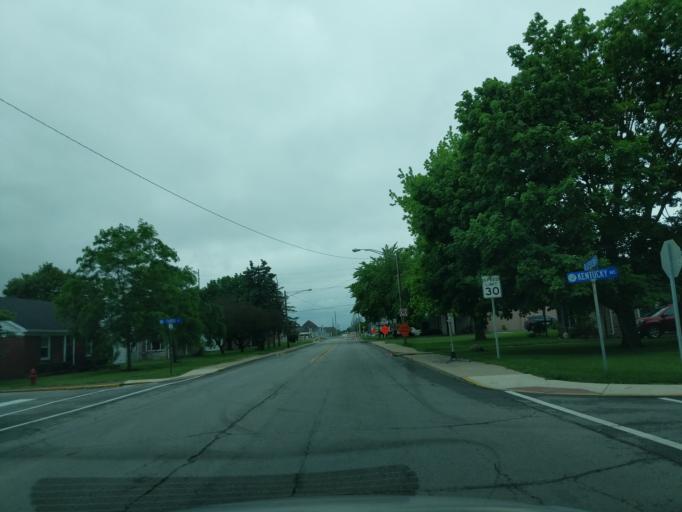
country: US
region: Indiana
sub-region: Tipton County
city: Tipton
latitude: 40.2820
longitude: -86.0486
